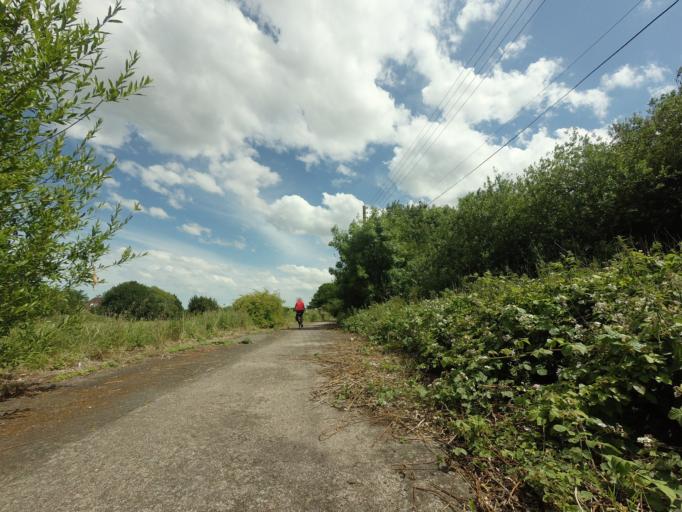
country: GB
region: England
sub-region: Medway
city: High Halstow
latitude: 51.4448
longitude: 0.5785
